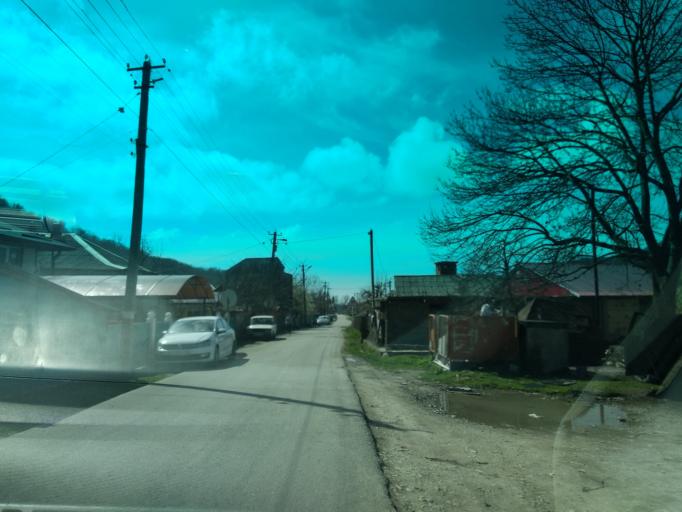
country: RU
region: Krasnodarskiy
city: Shepsi
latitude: 44.0522
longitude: 39.1623
